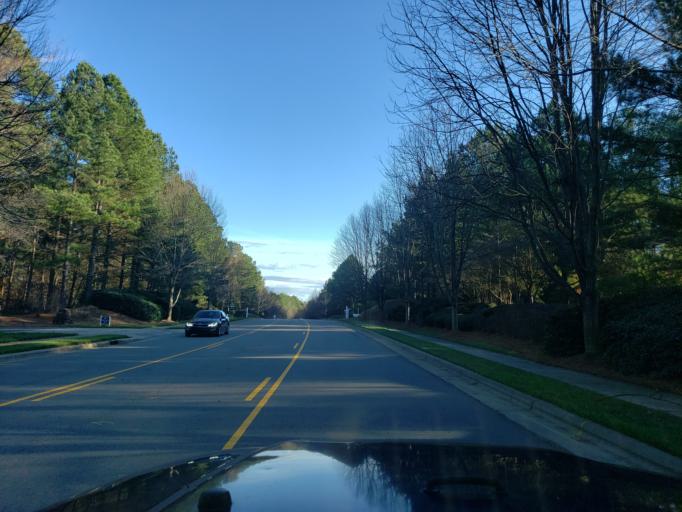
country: US
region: North Carolina
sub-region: Catawba County
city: Lake Norman of Catawba
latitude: 35.5471
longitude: -80.9212
